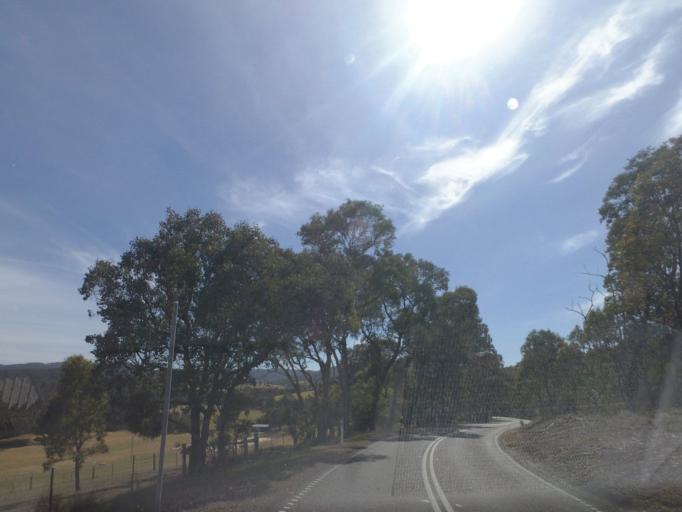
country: AU
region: Victoria
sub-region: Nillumbik
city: Saint Andrews
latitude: -37.5790
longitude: 145.2880
